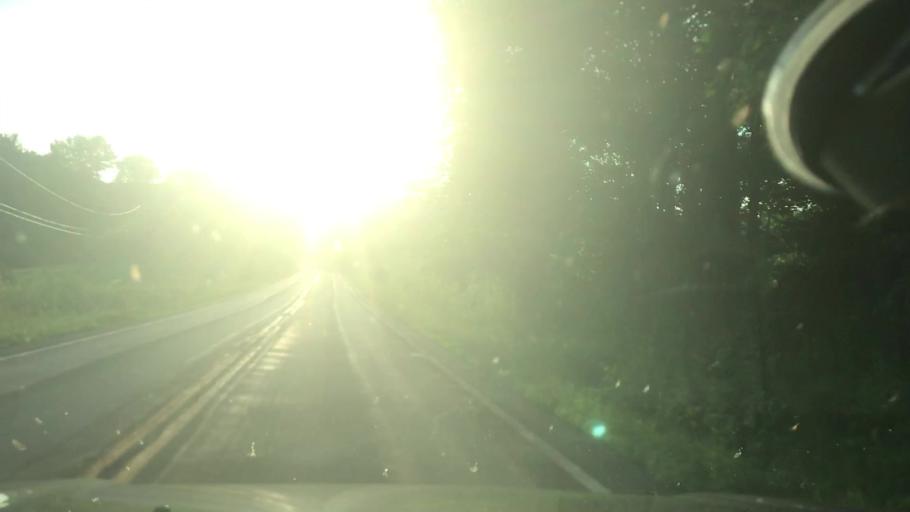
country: US
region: New York
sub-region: Otsego County
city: Unadilla
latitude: 42.3401
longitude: -75.2560
